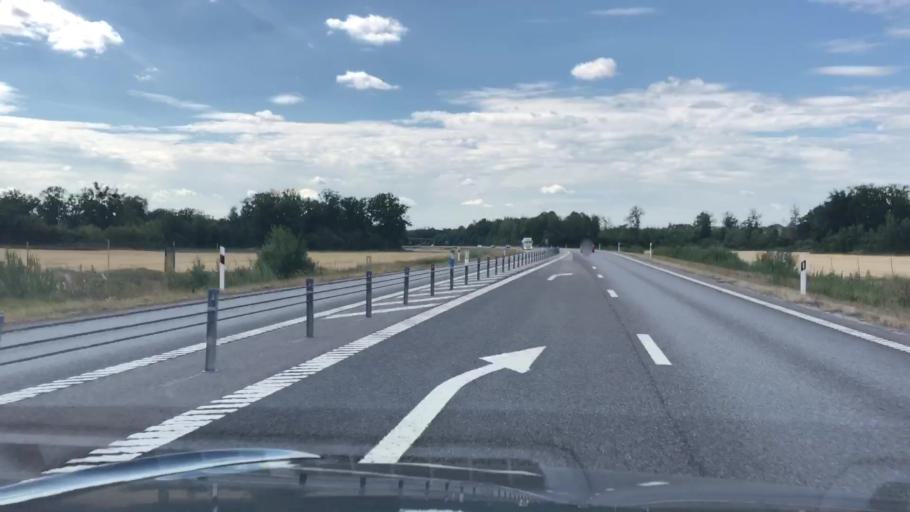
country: SE
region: Kalmar
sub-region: Kalmar Kommun
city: Ljungbyholm
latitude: 56.5695
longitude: 16.0962
